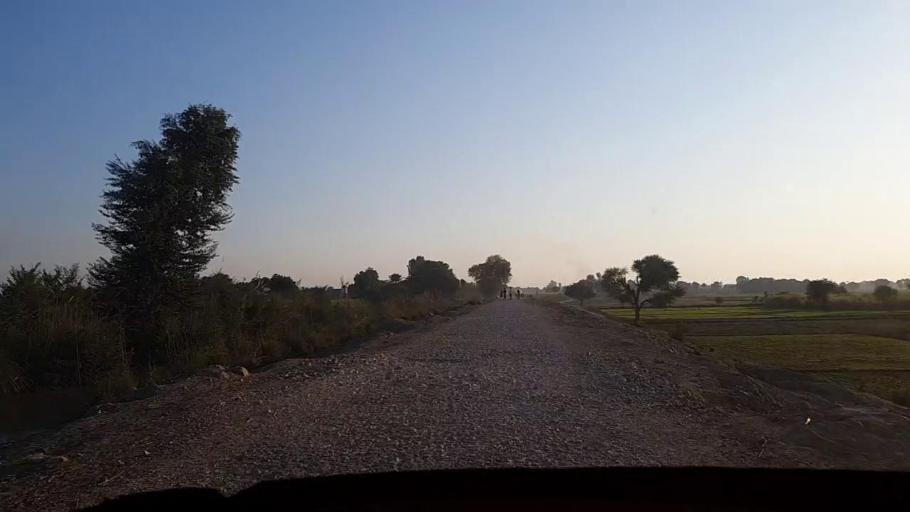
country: PK
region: Sindh
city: Sobhadero
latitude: 27.3708
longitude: 68.3779
